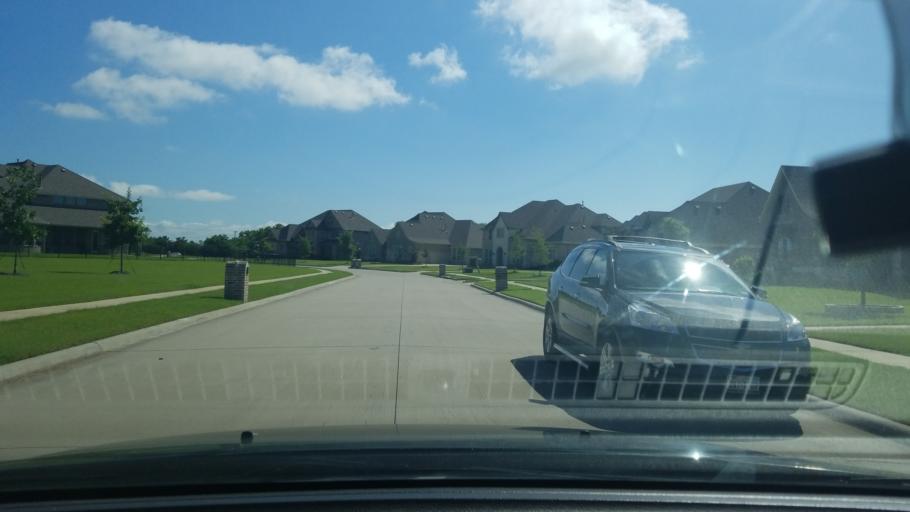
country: US
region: Texas
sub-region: Dallas County
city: Sunnyvale
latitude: 32.8120
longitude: -96.5717
